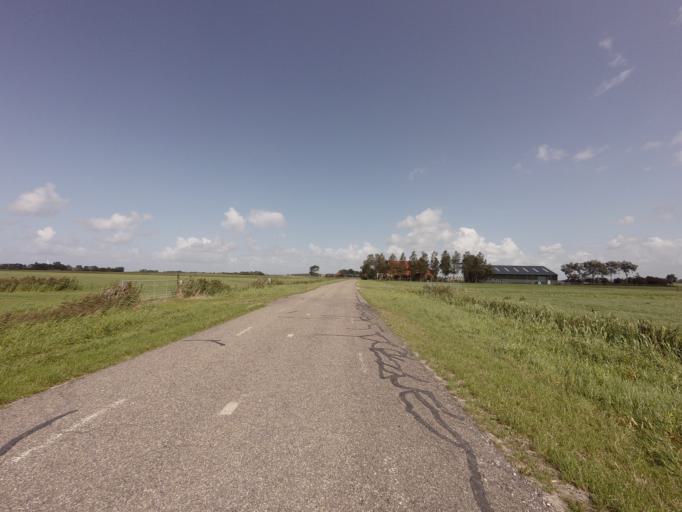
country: NL
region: Friesland
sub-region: Sudwest Fryslan
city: Makkum
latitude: 53.1036
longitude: 5.4305
